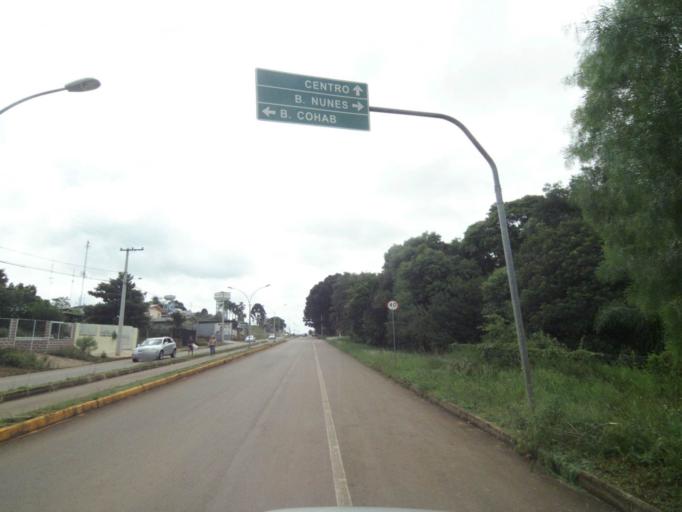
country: BR
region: Rio Grande do Sul
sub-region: Lagoa Vermelha
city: Lagoa Vermelha
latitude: -28.2231
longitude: -51.5107
